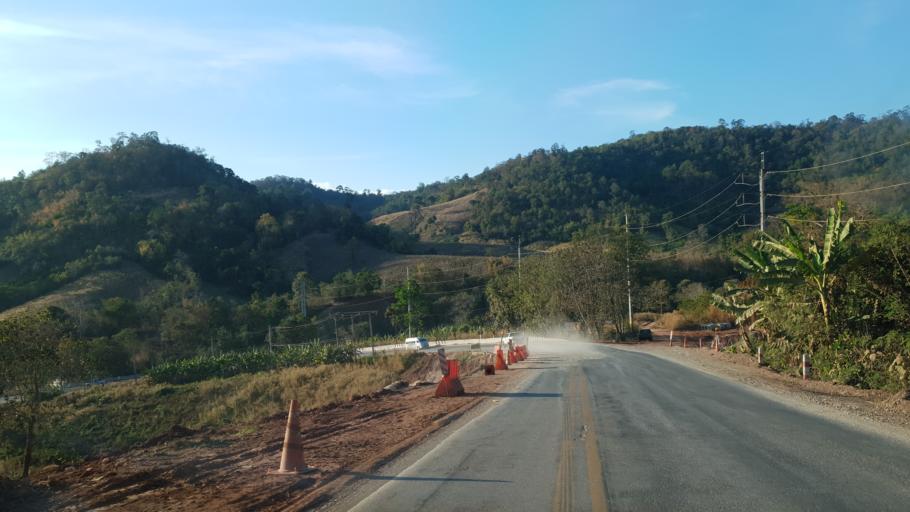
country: TH
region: Loei
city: Dan Sai
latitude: 17.2307
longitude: 101.0775
